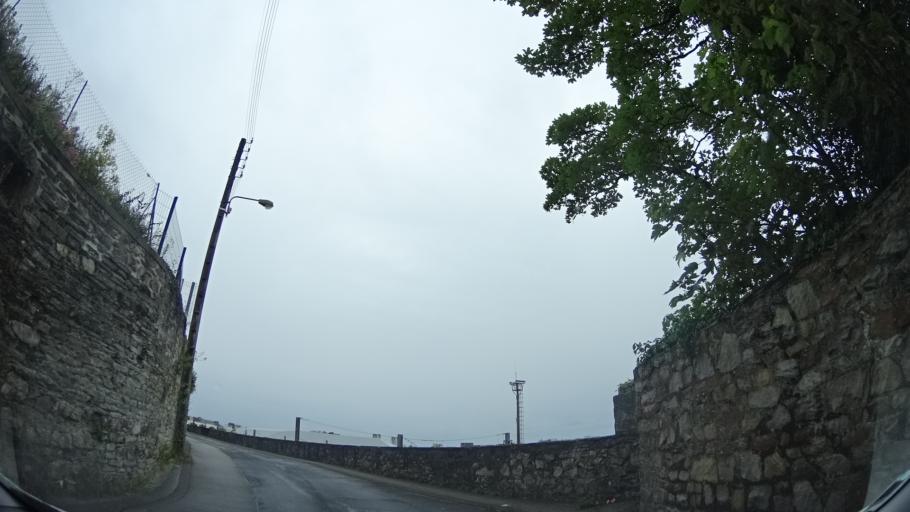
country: FR
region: Lower Normandy
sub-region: Departement de la Manche
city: Cherbourg-Octeville
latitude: 49.6312
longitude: -1.6192
